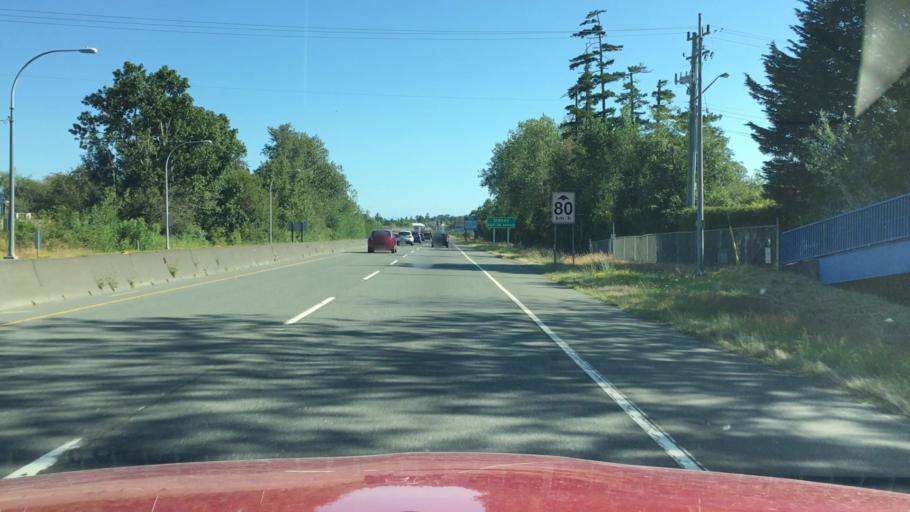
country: CA
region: British Columbia
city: North Saanich
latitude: 48.6410
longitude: -123.4069
